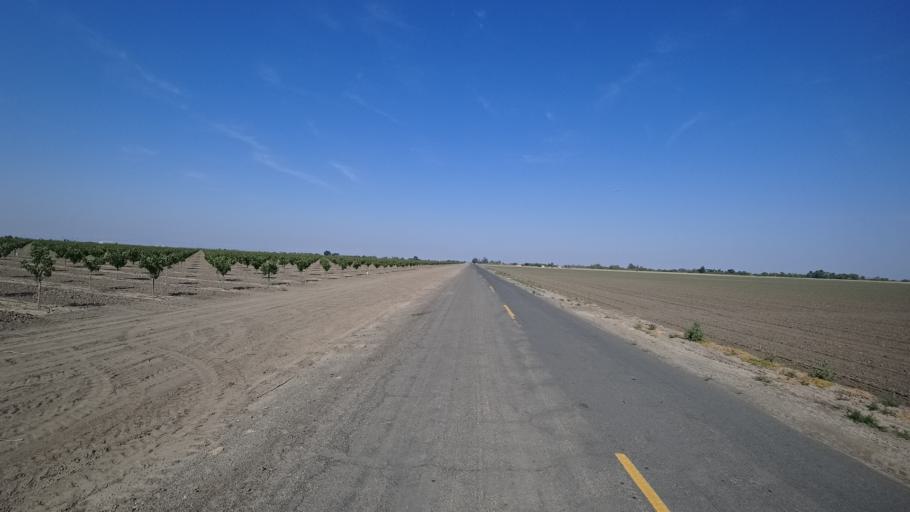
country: US
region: California
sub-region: Kings County
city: Lemoore Station
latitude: 36.3285
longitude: -119.8635
